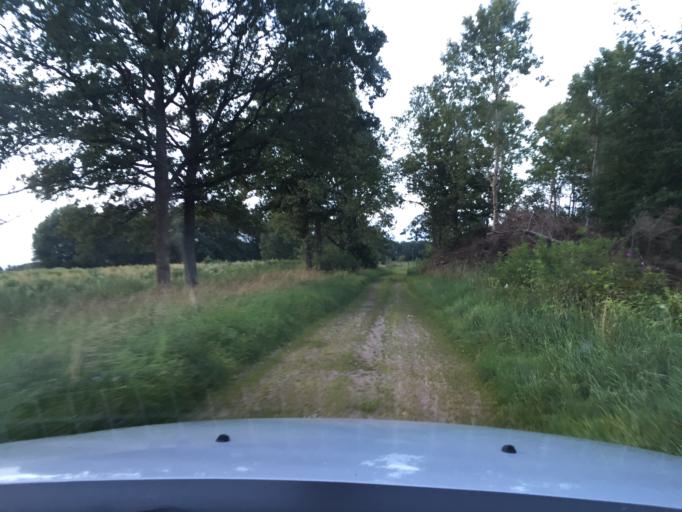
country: SE
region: Skane
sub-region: Hassleholms Kommun
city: Sosdala
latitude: 56.0336
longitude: 13.6892
